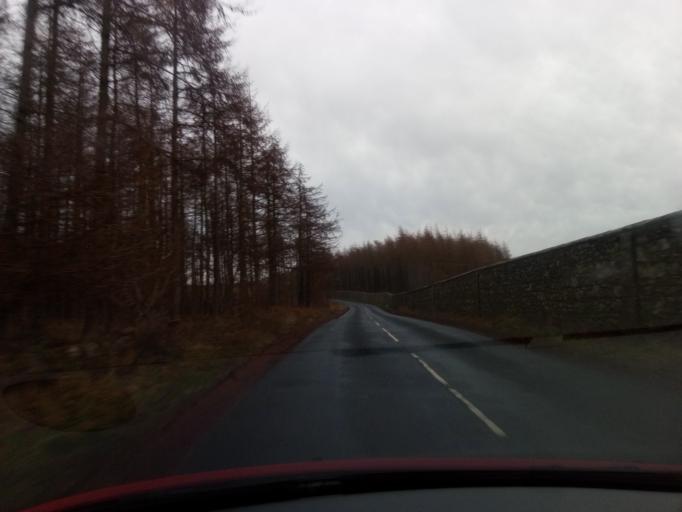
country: GB
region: England
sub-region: Northumberland
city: Alnwick
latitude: 55.4449
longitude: -1.7434
